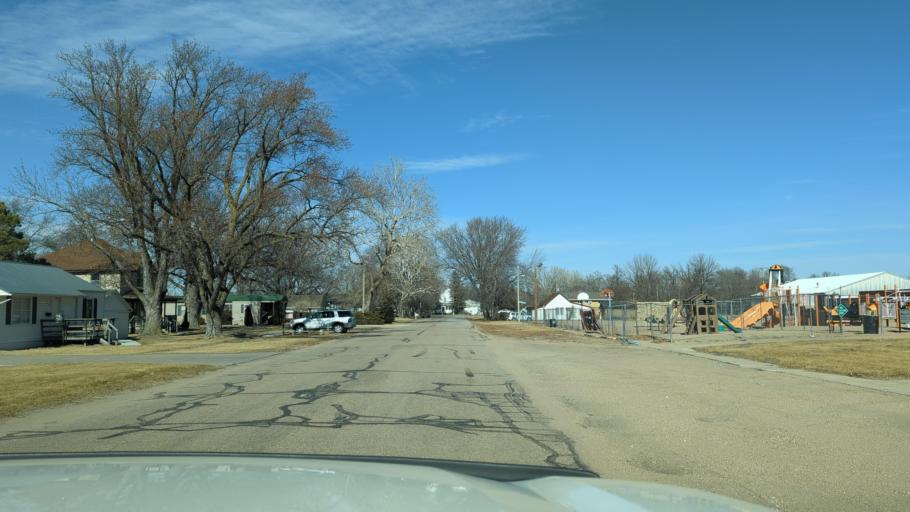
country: US
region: Nebraska
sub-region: Antelope County
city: Neligh
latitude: 42.2607
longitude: -98.3451
